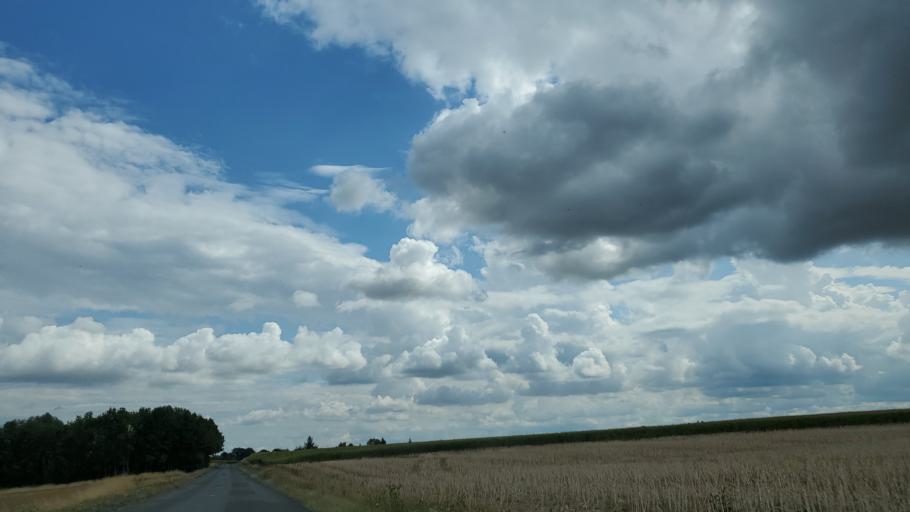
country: FR
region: Ile-de-France
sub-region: Departement de Seine-et-Marne
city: Mouroux
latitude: 48.8385
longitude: 3.0315
